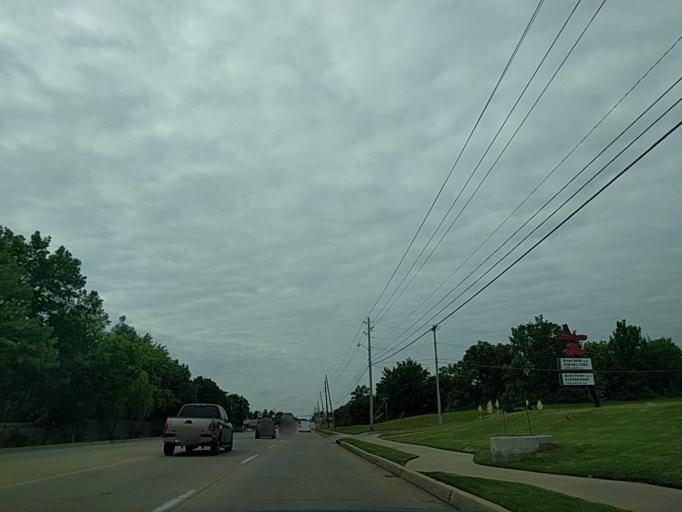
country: US
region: Oklahoma
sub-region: Tulsa County
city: Jenks
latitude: 36.0658
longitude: -95.9044
